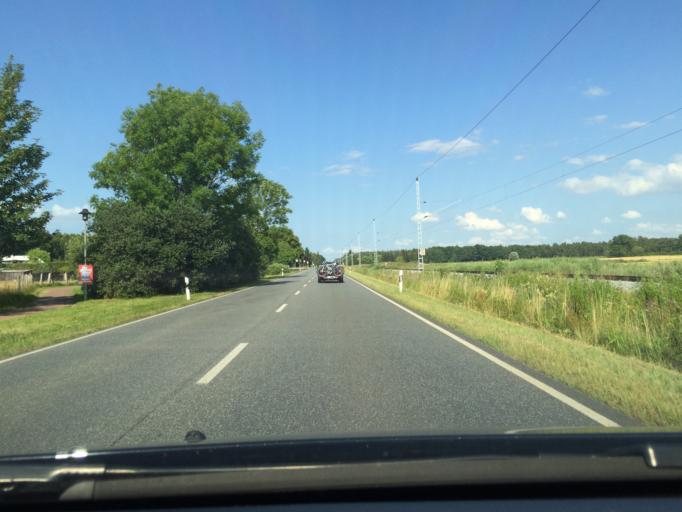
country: DE
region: Mecklenburg-Vorpommern
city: Rovershagen
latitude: 54.1790
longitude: 12.2540
